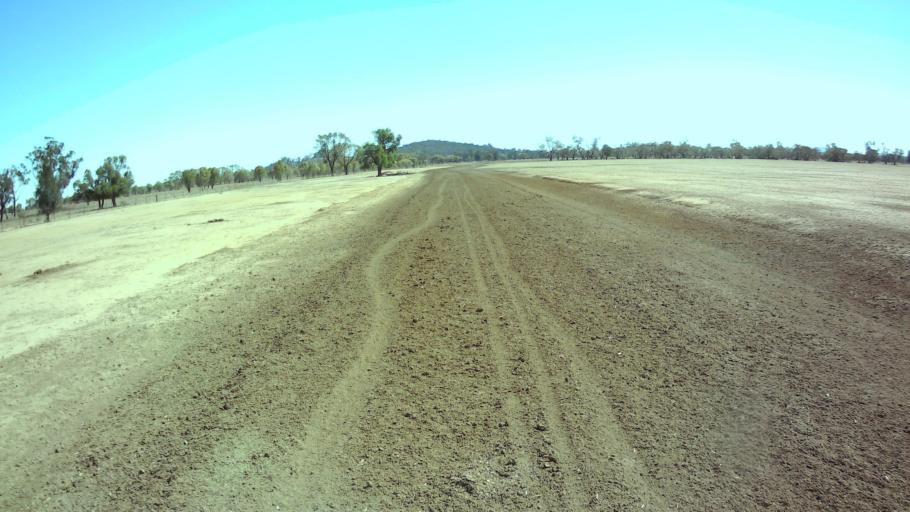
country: AU
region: New South Wales
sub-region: Bland
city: West Wyalong
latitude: -33.7553
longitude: 147.6593
